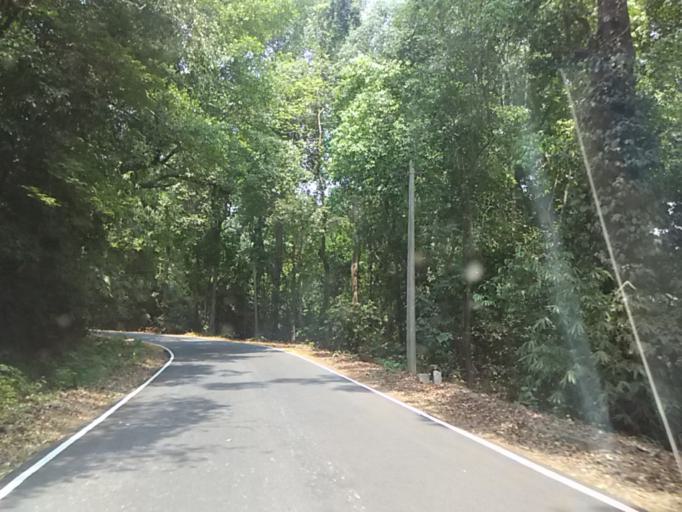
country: IN
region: Karnataka
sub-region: Kodagu
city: Virarajendrapet
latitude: 12.0780
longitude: 75.7329
